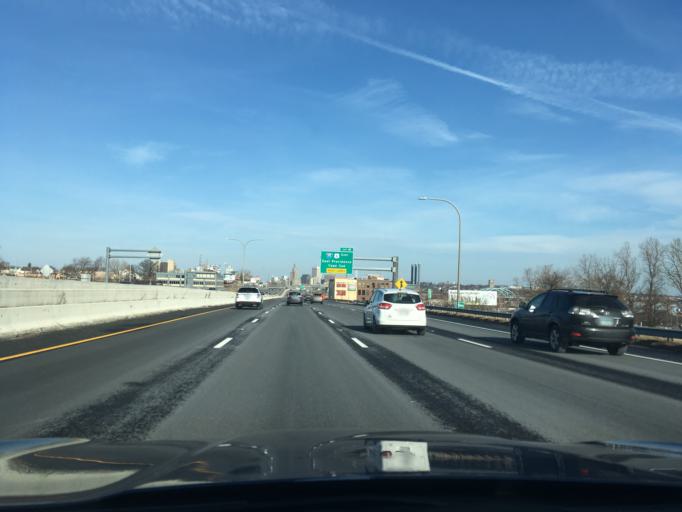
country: US
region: Rhode Island
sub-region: Providence County
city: Providence
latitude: 41.8005
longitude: -71.4029
